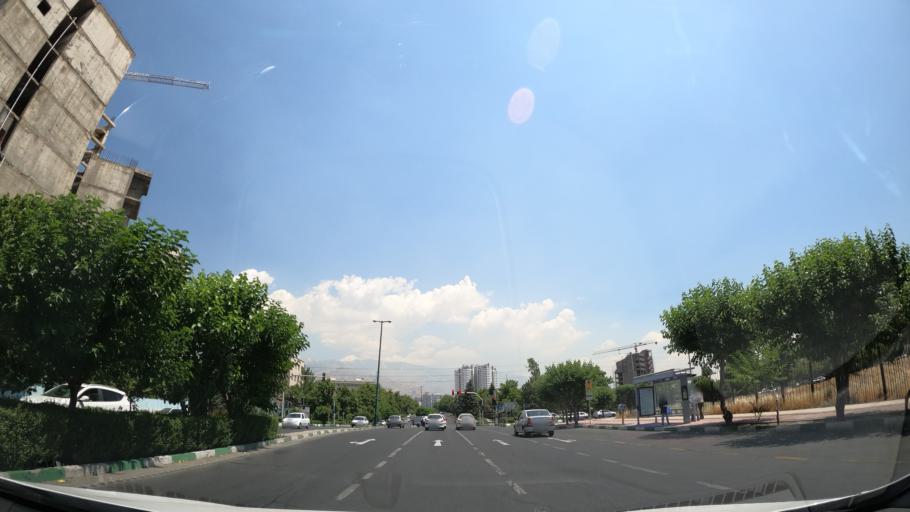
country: IR
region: Tehran
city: Tajrish
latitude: 35.7613
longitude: 51.3755
